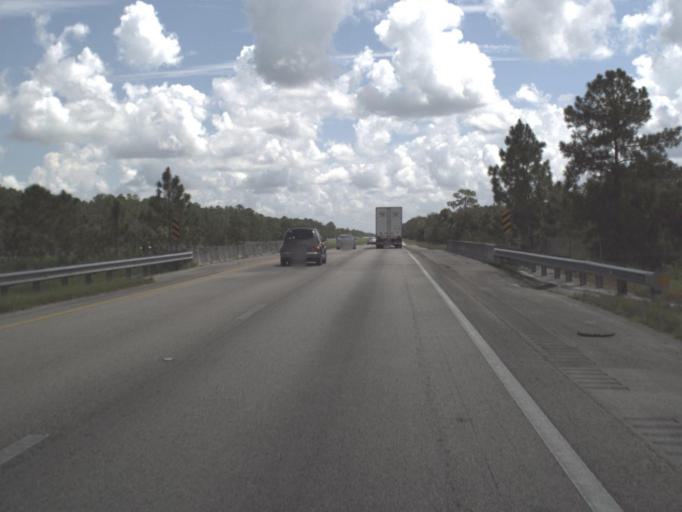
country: US
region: Florida
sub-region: Collier County
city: Orangetree
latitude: 26.1531
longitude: -81.4679
